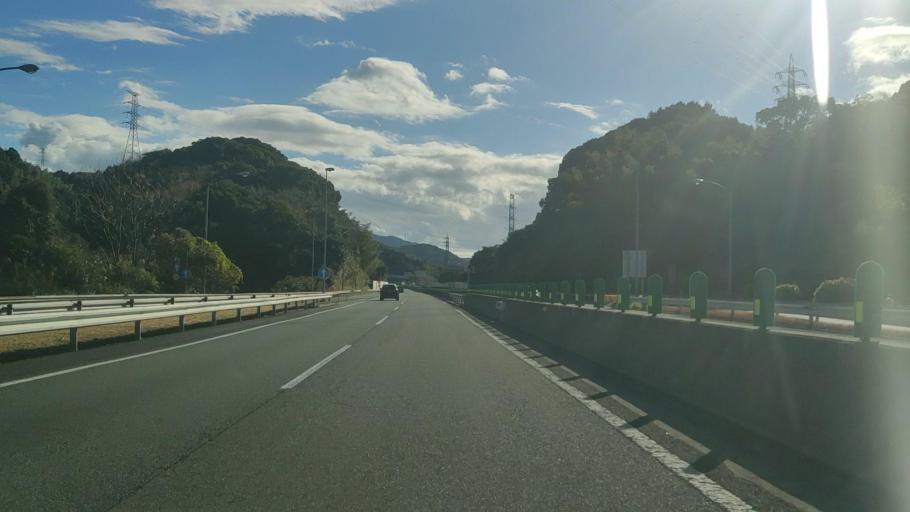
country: JP
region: Fukuoka
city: Kitakyushu
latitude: 33.8400
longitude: 130.7653
